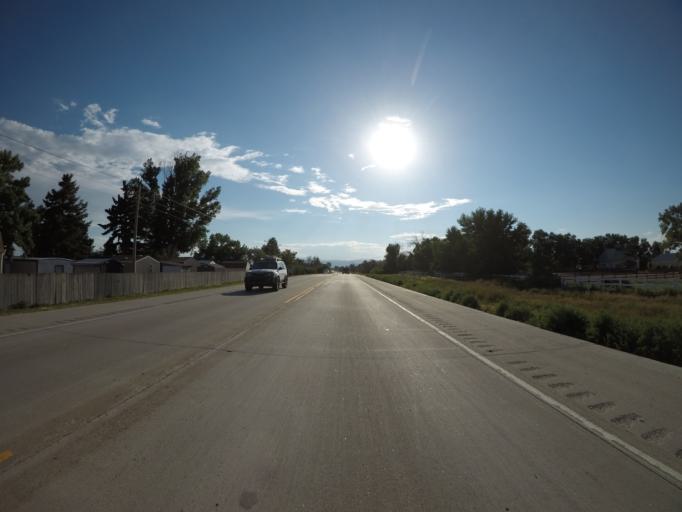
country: US
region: Colorado
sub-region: Weld County
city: Severance
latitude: 40.5816
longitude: -104.9218
